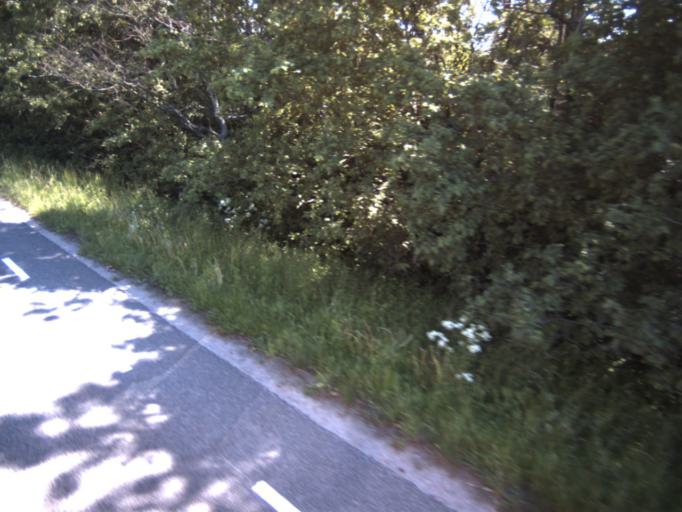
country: SE
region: Skane
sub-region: Helsingborg
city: Barslov
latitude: 56.0088
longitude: 12.7943
